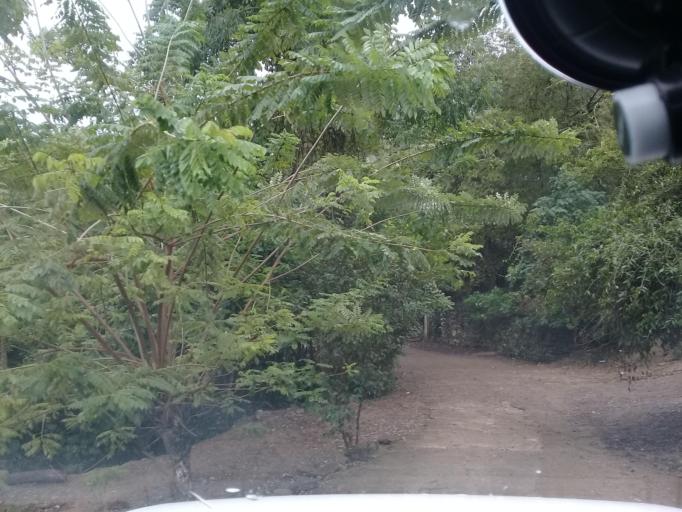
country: MX
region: Veracruz
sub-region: Chalma
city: San Pedro Coyutla
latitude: 21.2494
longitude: -98.4149
